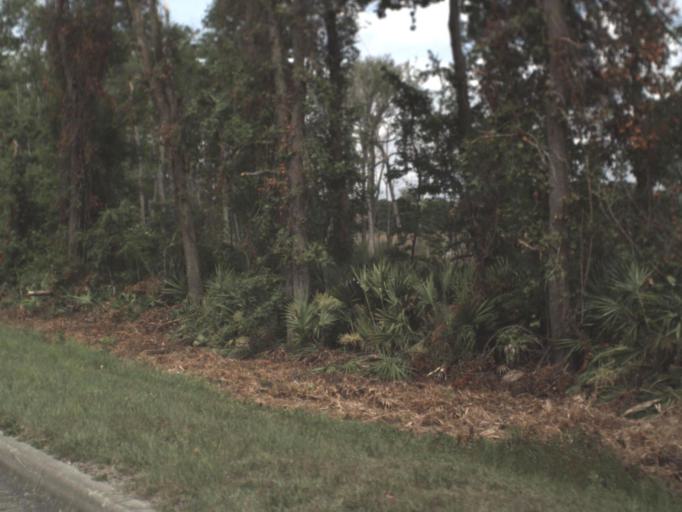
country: US
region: Florida
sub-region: Duval County
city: Jacksonville
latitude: 30.4083
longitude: -81.6268
